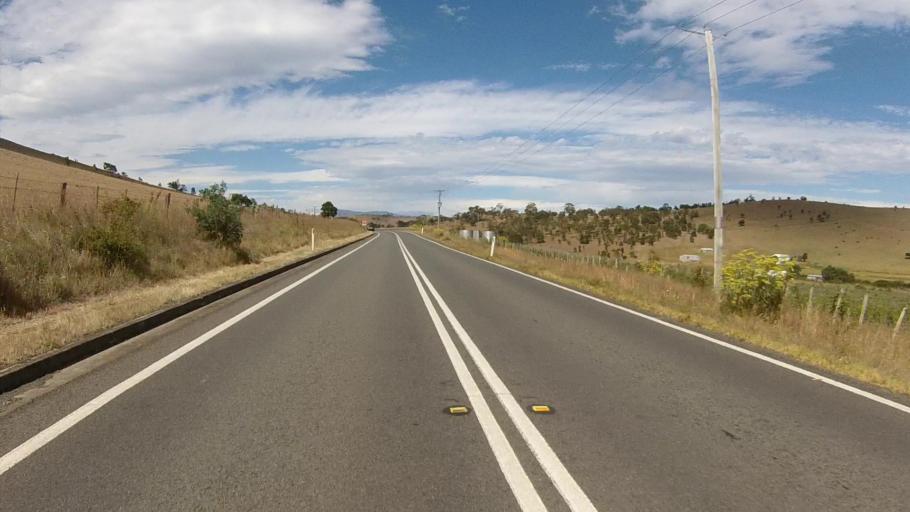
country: AU
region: Tasmania
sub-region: Brighton
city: Old Beach
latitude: -42.6787
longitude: 147.3551
